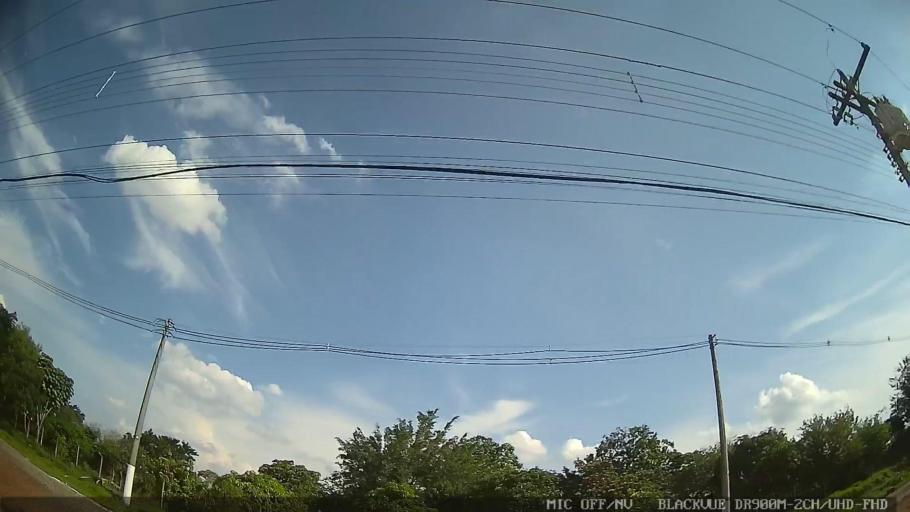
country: BR
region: Sao Paulo
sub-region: Braganca Paulista
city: Braganca Paulista
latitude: -22.9489
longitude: -46.5259
